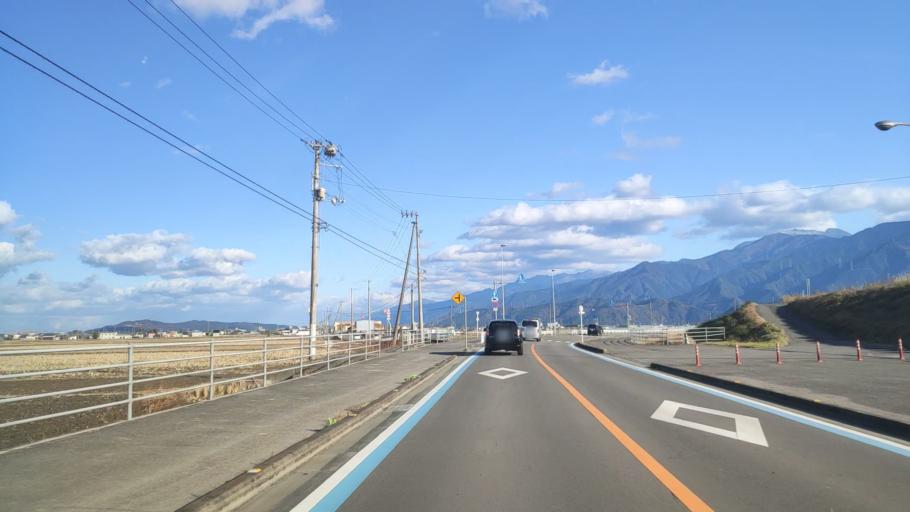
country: JP
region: Ehime
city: Saijo
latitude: 33.9094
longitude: 133.1402
